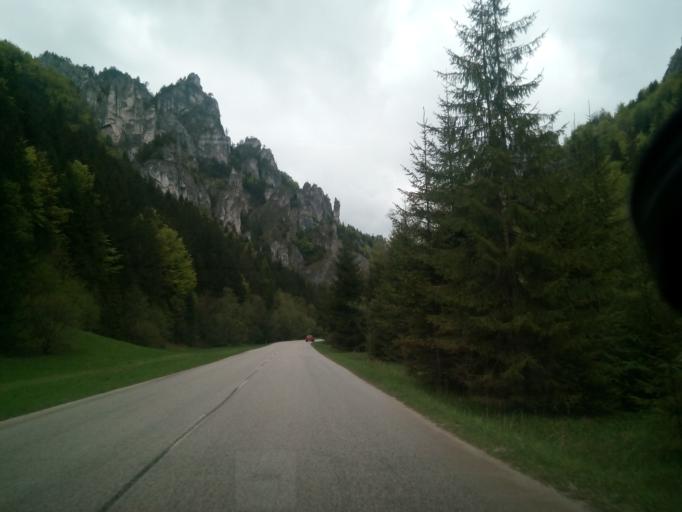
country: SK
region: Zilinsky
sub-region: Okres Zilina
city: Terchova
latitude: 49.2395
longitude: 19.0405
